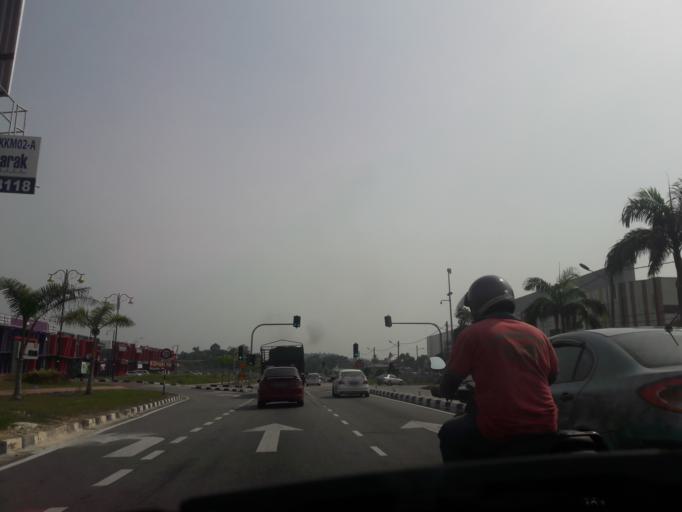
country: MY
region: Kedah
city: Kulim
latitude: 5.3844
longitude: 100.5456
